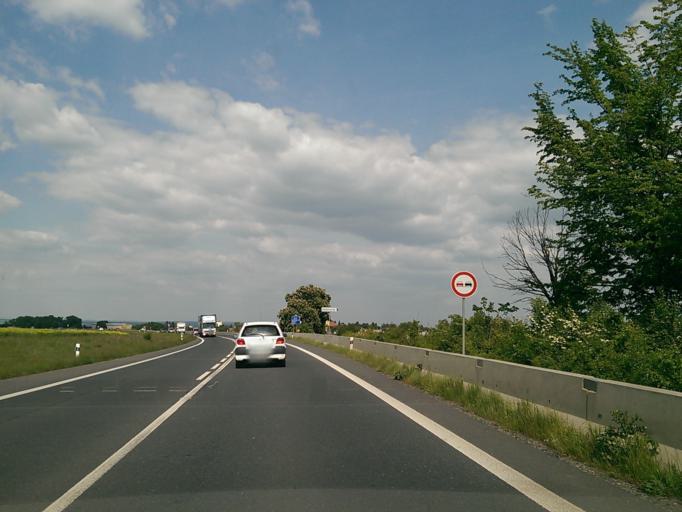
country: CZ
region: Central Bohemia
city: Libeznice
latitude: 50.1862
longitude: 14.4791
